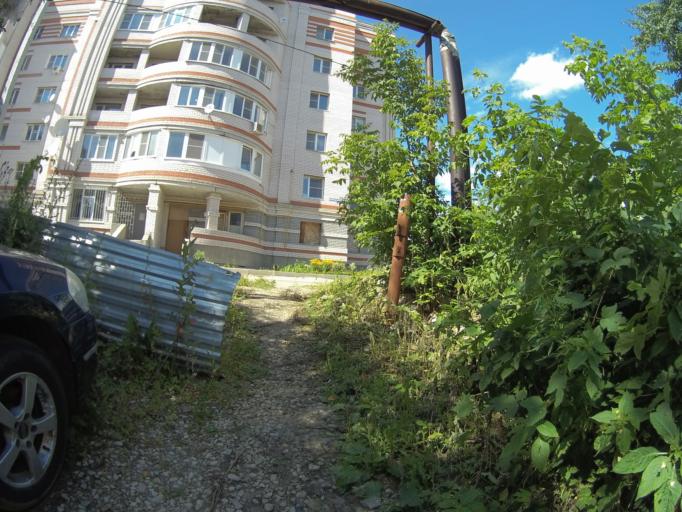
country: RU
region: Vladimir
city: Vladimir
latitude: 56.1376
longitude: 40.4175
